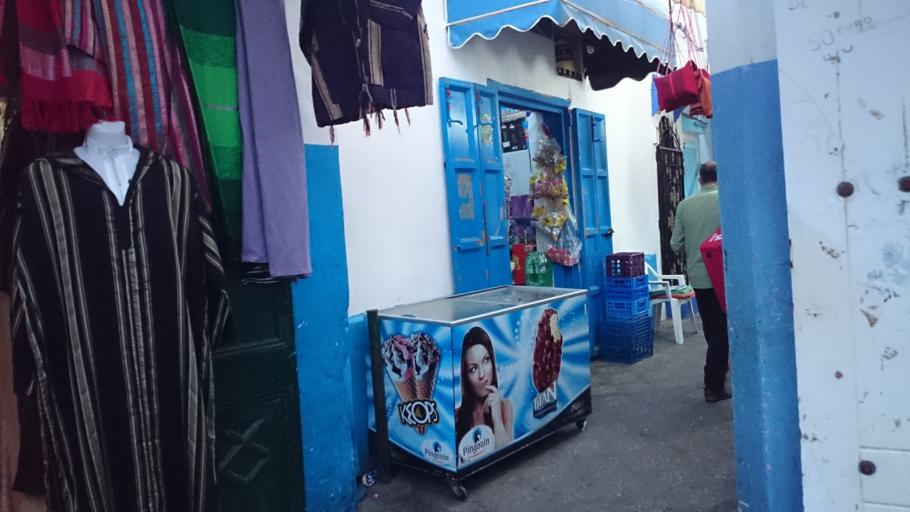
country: MA
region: Tanger-Tetouan
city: Asilah
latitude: 35.4656
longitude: -6.0387
